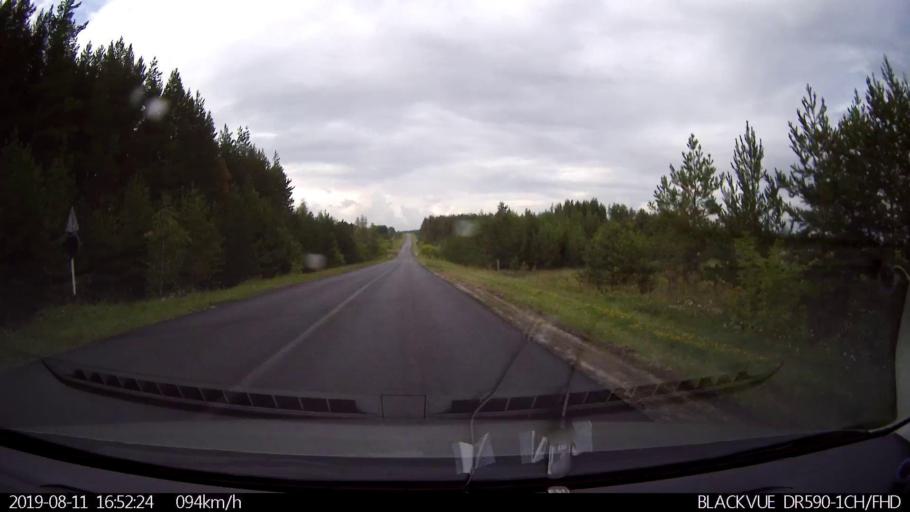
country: RU
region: Ulyanovsk
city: Mayna
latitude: 54.2478
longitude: 47.6742
